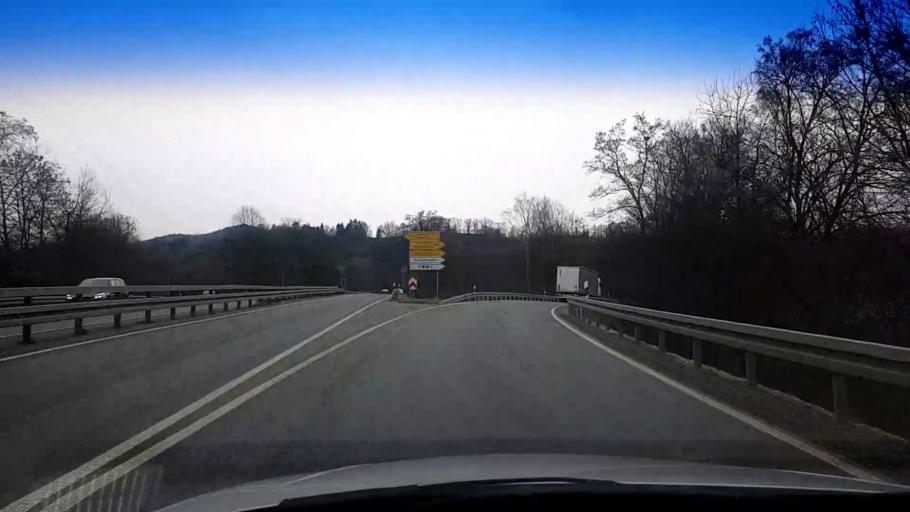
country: DE
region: Bavaria
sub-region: Upper Franconia
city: Kulmbach
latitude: 50.1066
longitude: 11.4328
